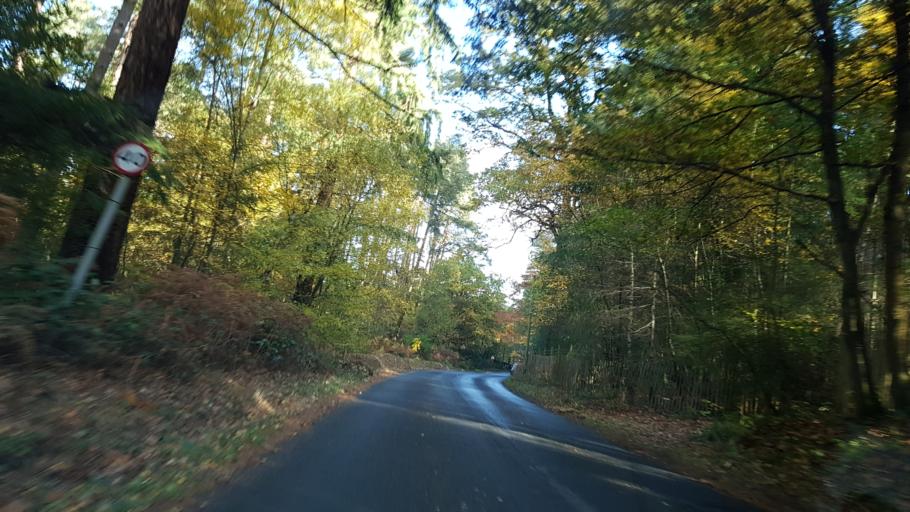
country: GB
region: England
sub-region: Surrey
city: Churt
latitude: 51.1468
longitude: -0.7545
